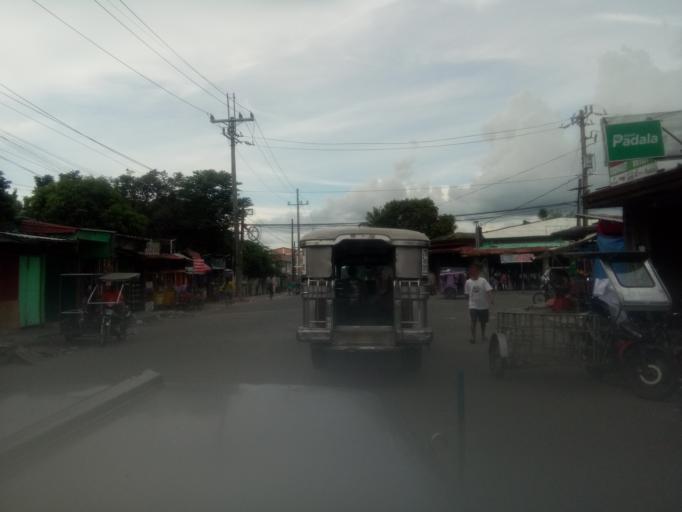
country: PH
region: Calabarzon
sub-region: Province of Cavite
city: Bulihan
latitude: 14.2844
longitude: 120.9990
